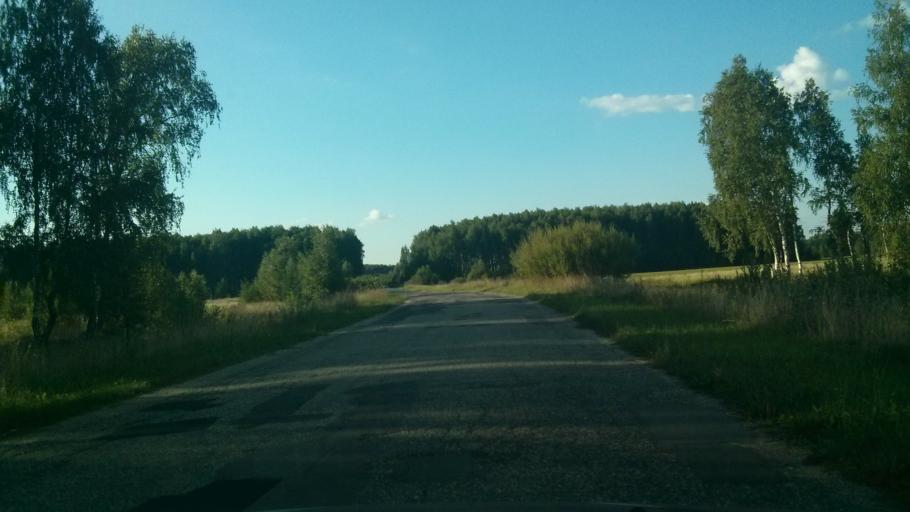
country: RU
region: Vladimir
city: Melenki
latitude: 55.3248
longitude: 41.7774
